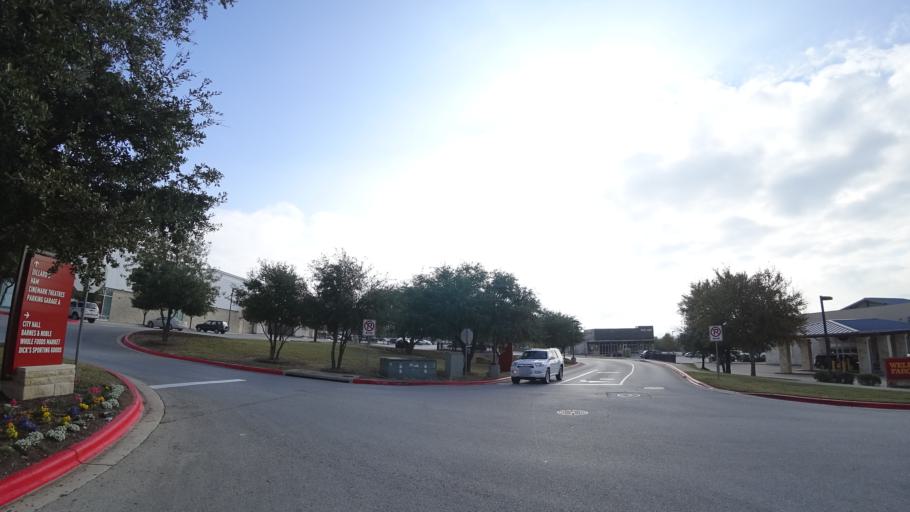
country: US
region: Texas
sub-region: Travis County
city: Bee Cave
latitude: 30.3094
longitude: -97.9436
